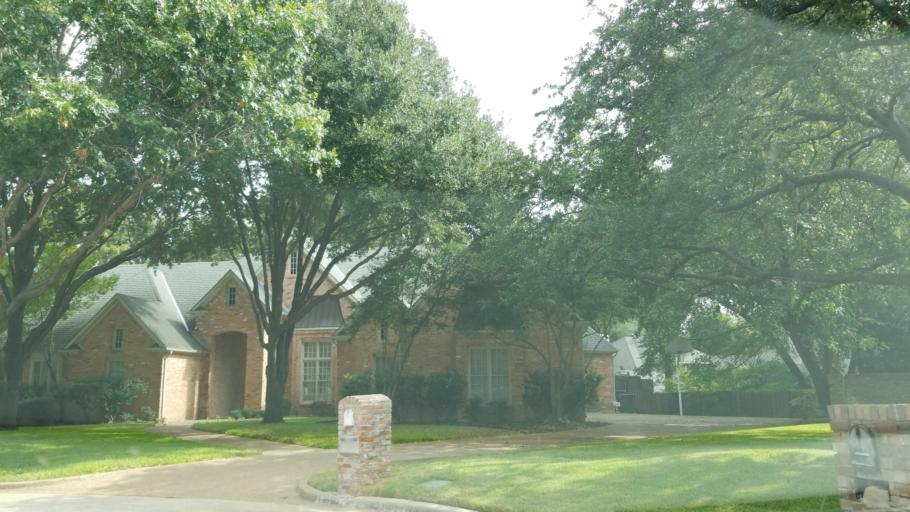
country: US
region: Texas
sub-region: Dallas County
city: Addison
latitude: 32.9394
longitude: -96.8004
